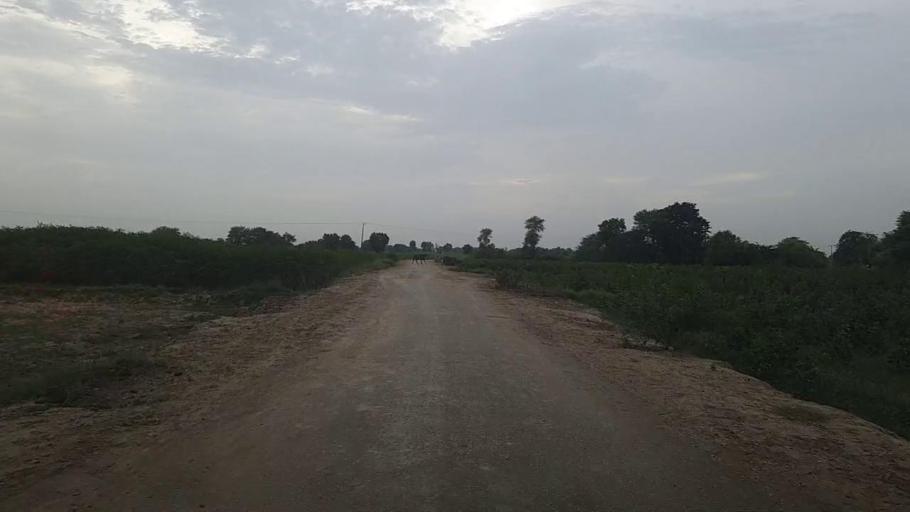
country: PK
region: Sindh
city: Karaundi
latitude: 26.9572
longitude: 68.3589
